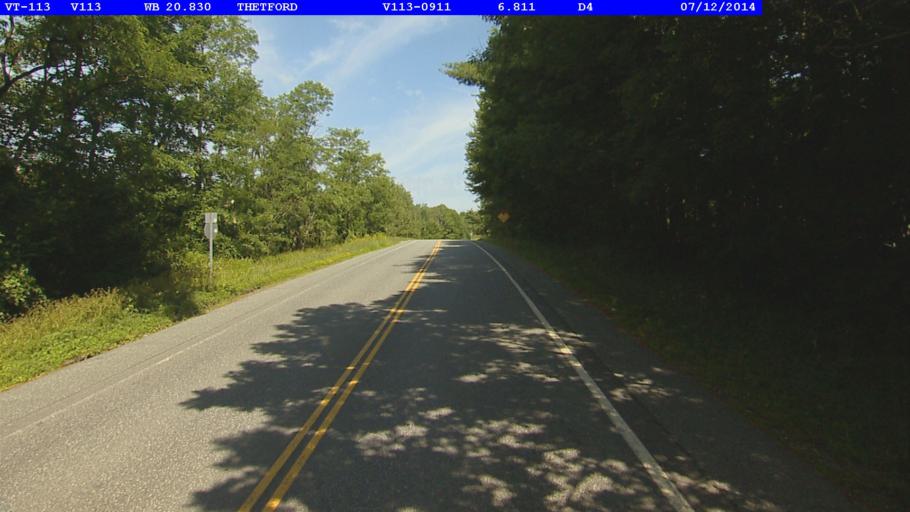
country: US
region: New Hampshire
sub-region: Grafton County
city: Lyme
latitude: 43.8146
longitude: -72.2198
